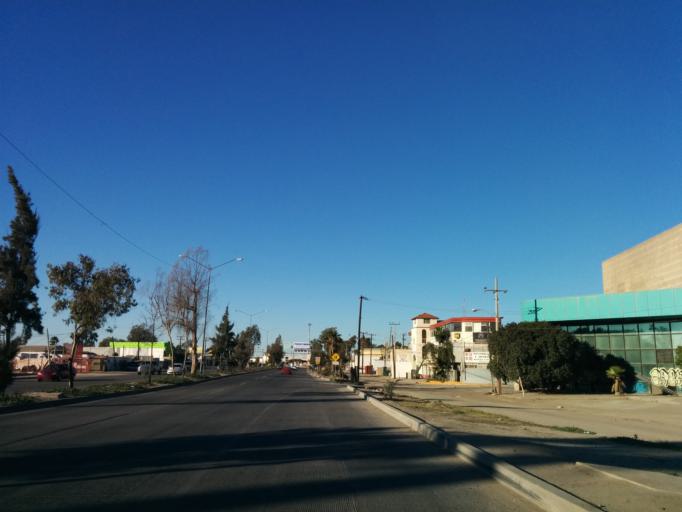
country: MX
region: Baja California
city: Tijuana
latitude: 32.5443
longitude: -116.9476
